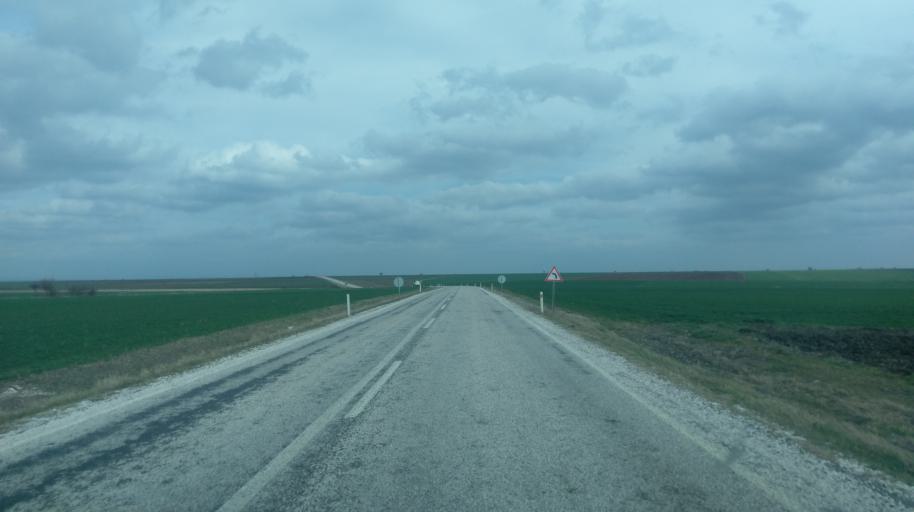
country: TR
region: Edirne
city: Haskoy
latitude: 41.6496
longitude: 26.8838
